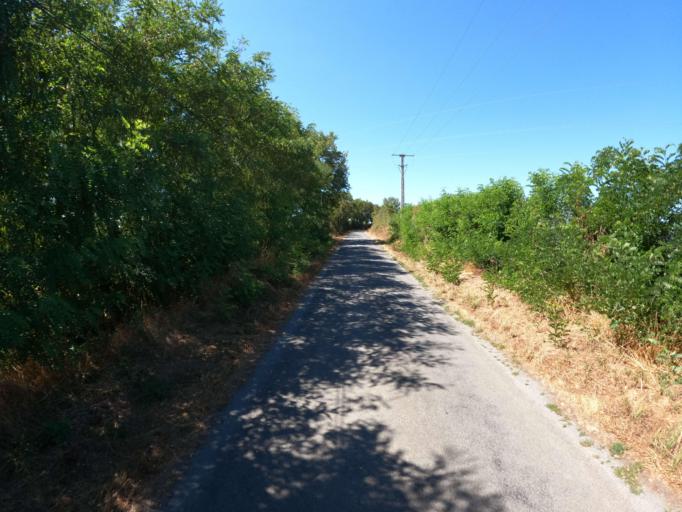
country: FR
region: Pays de la Loire
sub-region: Departement de Maine-et-Loire
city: Saint-Christophe-du-Bois
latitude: 47.0381
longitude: -0.9522
